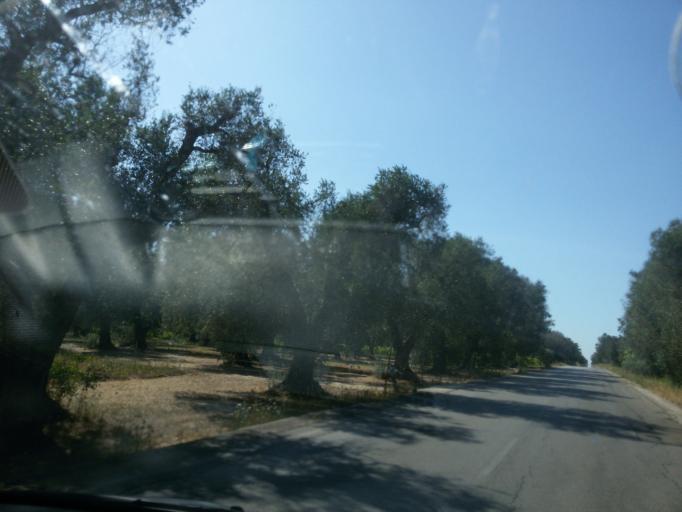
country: IT
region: Apulia
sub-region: Provincia di Brindisi
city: San Donaci
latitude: 40.4700
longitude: 17.9004
